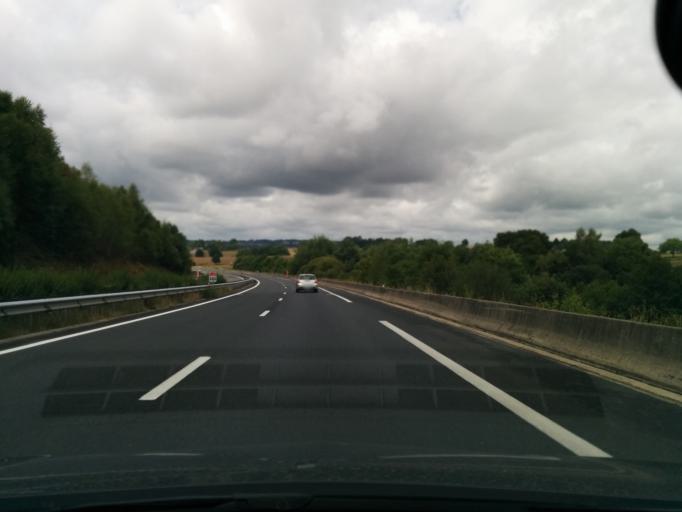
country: FR
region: Limousin
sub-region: Departement de la Correze
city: Uzerche
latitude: 45.4055
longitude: 1.5577
